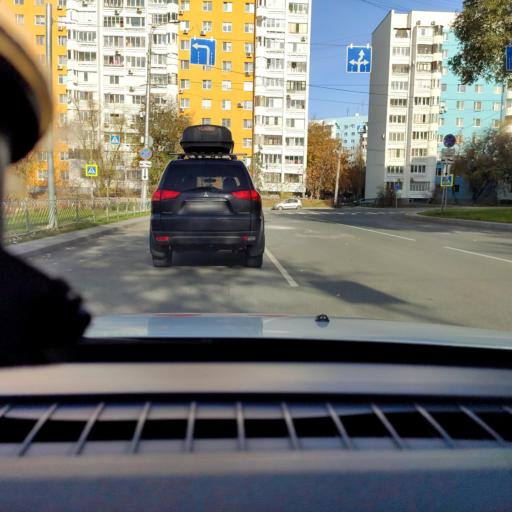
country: RU
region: Samara
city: Samara
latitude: 53.1889
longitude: 50.1365
